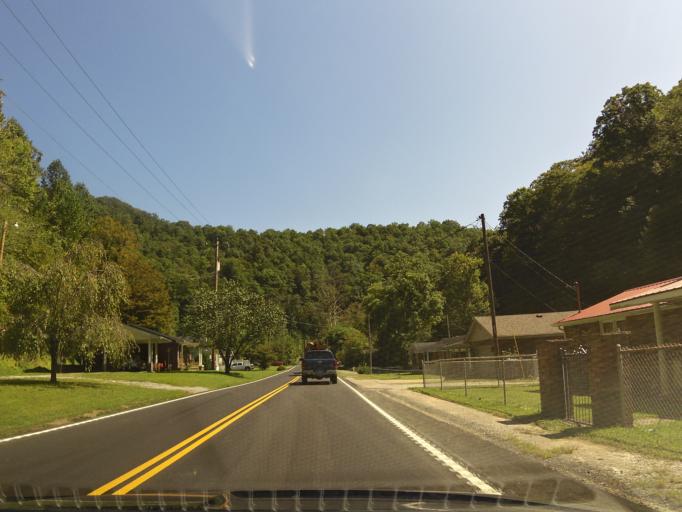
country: US
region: Kentucky
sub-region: Leslie County
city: Hyden
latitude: 37.1469
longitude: -83.4206
